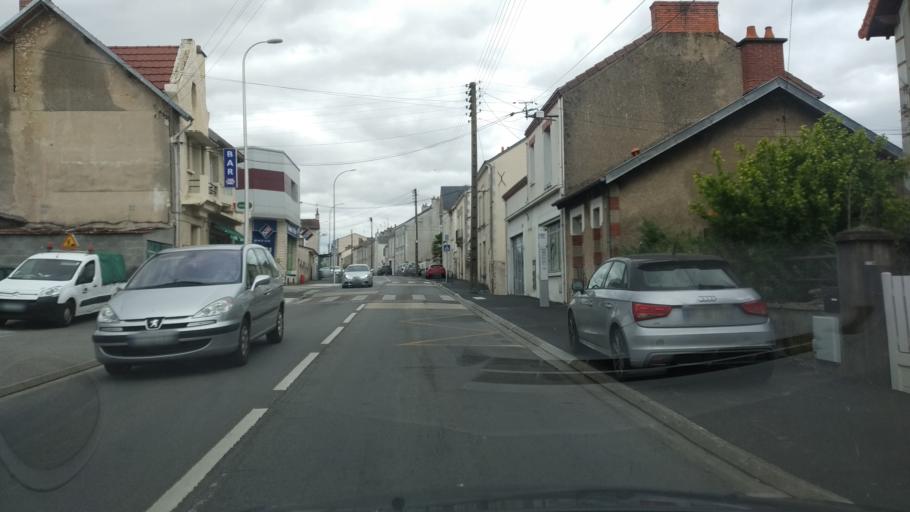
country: FR
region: Poitou-Charentes
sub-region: Departement de la Vienne
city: Poitiers
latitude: 46.5846
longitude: 0.3303
